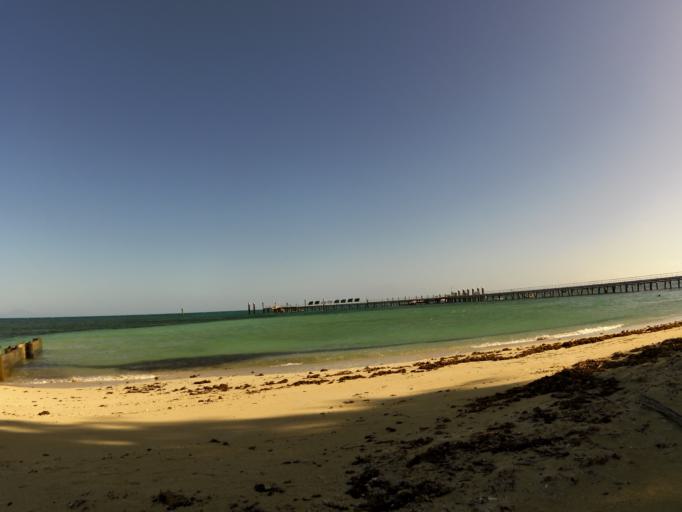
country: AU
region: Queensland
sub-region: Cairns
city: Yorkeys Knob
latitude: -16.7598
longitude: 145.9710
